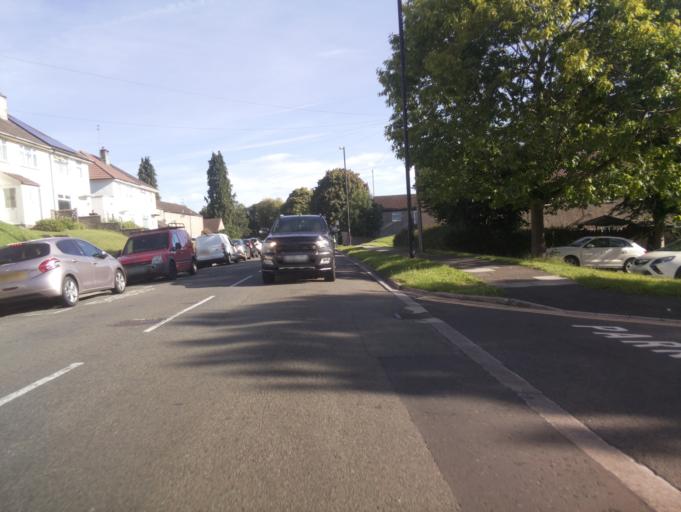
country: GB
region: England
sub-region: Bath and North East Somerset
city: Whitchurch
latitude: 51.4205
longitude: -2.5543
